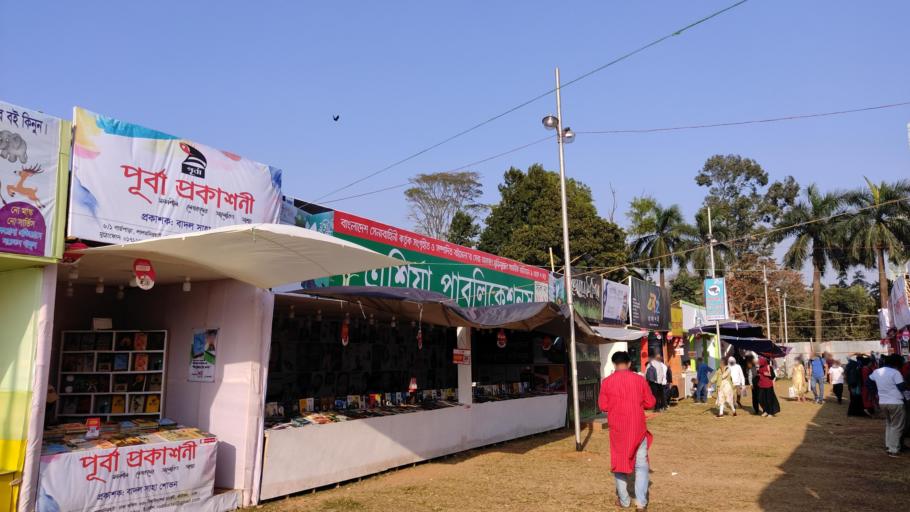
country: BD
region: Dhaka
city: Azimpur
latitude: 23.7331
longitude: 90.3994
